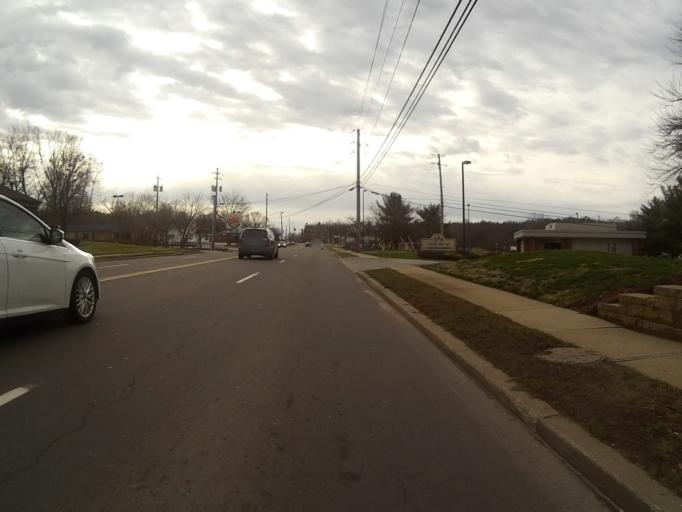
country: US
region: Ohio
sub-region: Portage County
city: Kent
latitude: 41.1380
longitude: -81.3558
